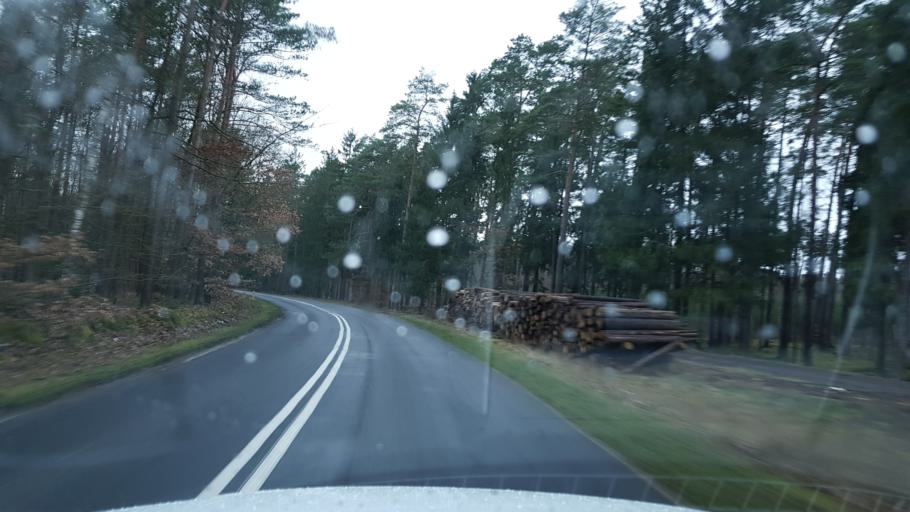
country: PL
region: West Pomeranian Voivodeship
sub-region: Powiat lobeski
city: Lobez
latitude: 53.6568
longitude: 15.5530
